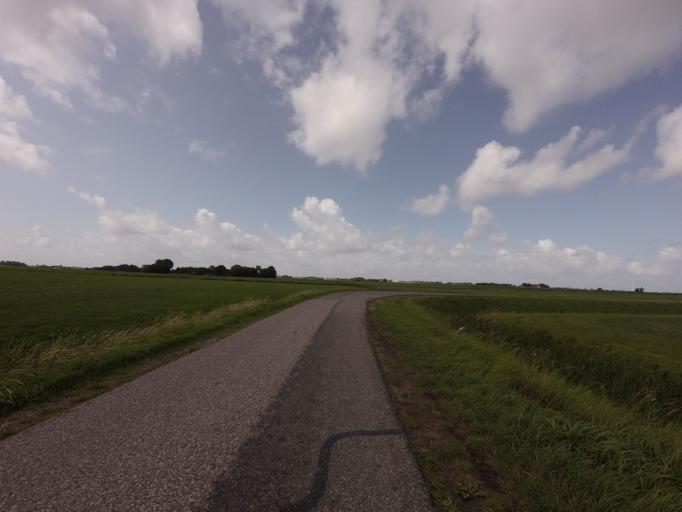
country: NL
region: Friesland
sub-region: Gemeente Franekeradeel
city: Sexbierum
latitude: 53.1656
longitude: 5.4853
